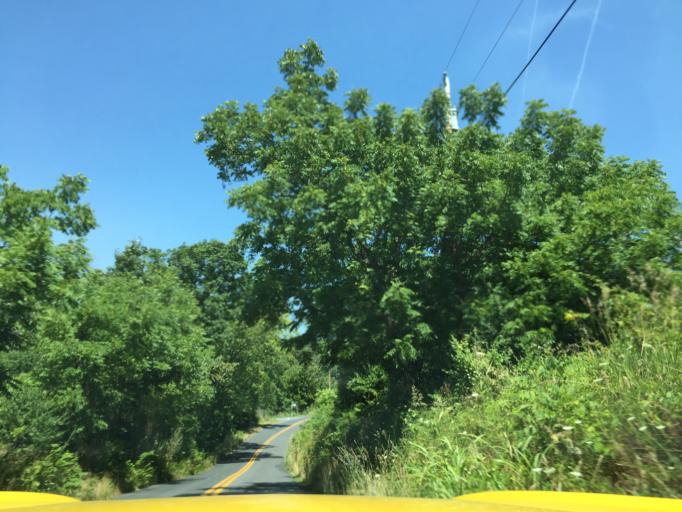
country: US
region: West Virginia
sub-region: Berkeley County
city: Inwood
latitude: 39.3305
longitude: -78.0354
